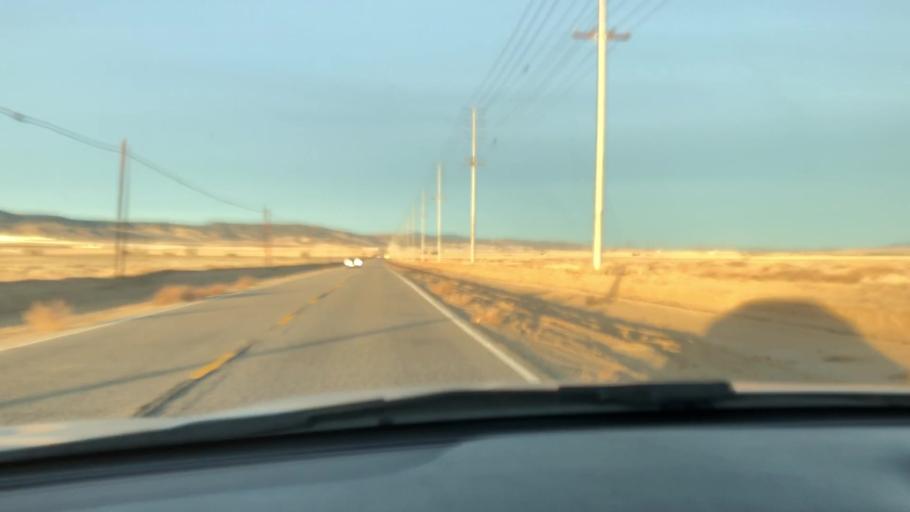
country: US
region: California
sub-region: Los Angeles County
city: Quartz Hill
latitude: 34.6749
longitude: -118.2636
